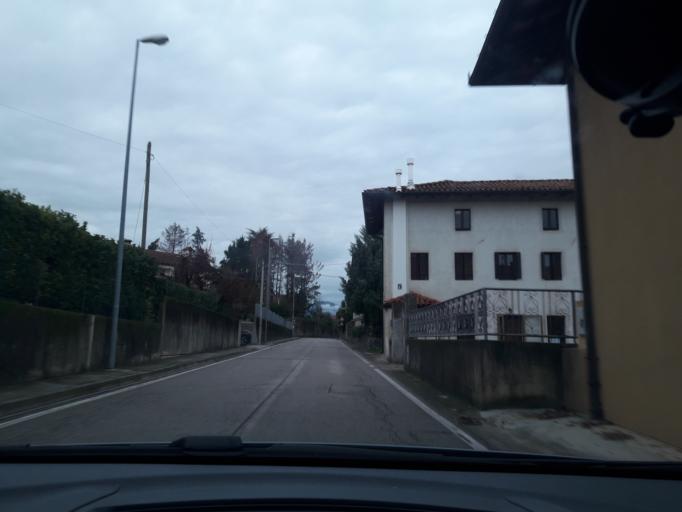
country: IT
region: Friuli Venezia Giulia
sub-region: Provincia di Udine
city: Reana del Rojale
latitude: 46.1340
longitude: 13.2419
